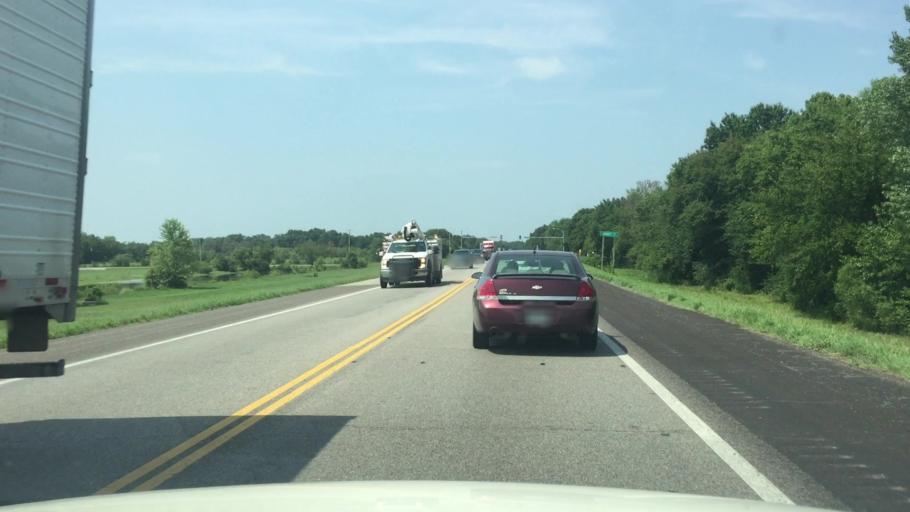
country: US
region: Kansas
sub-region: Crawford County
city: Pittsburg
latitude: 37.3941
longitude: -94.7178
